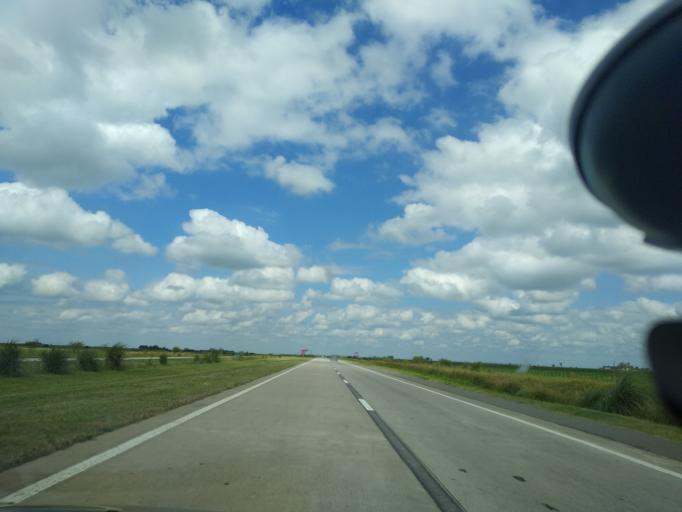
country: AR
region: Cordoba
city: Leones
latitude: -32.5986
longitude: -62.4660
